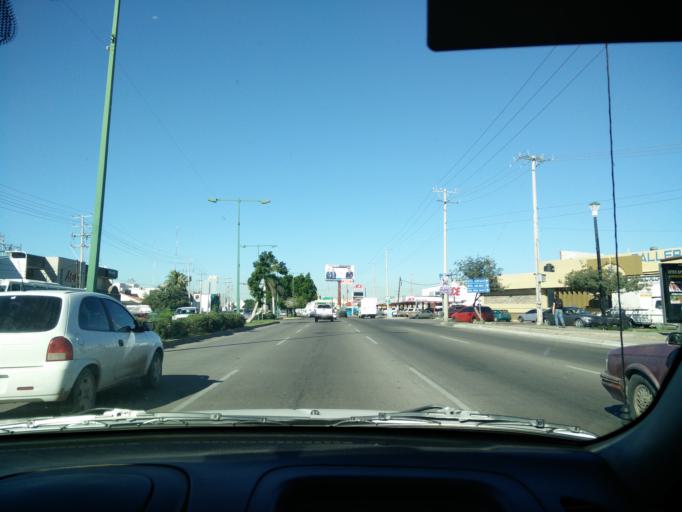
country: MX
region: Sonora
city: Hermosillo
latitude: 29.0929
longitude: -110.9778
